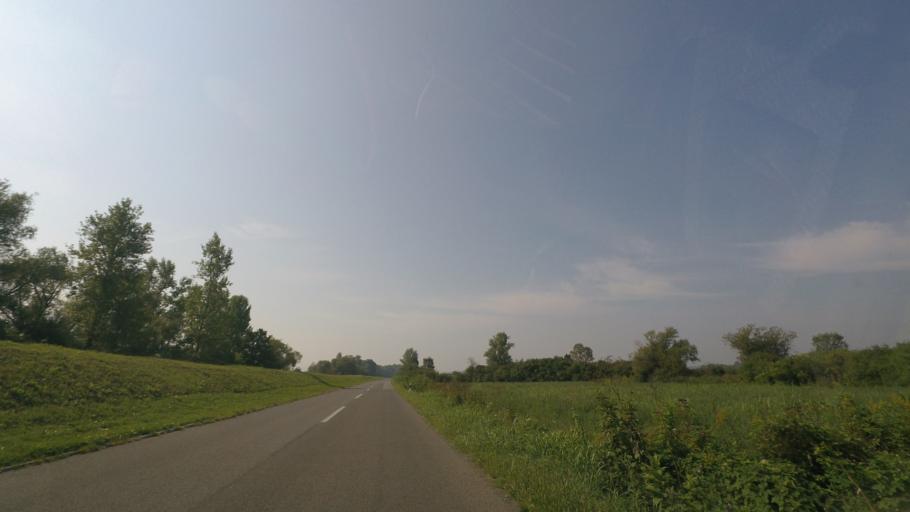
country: BA
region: Republika Srpska
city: Bosanska Dubica
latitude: 45.2273
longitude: 16.8363
